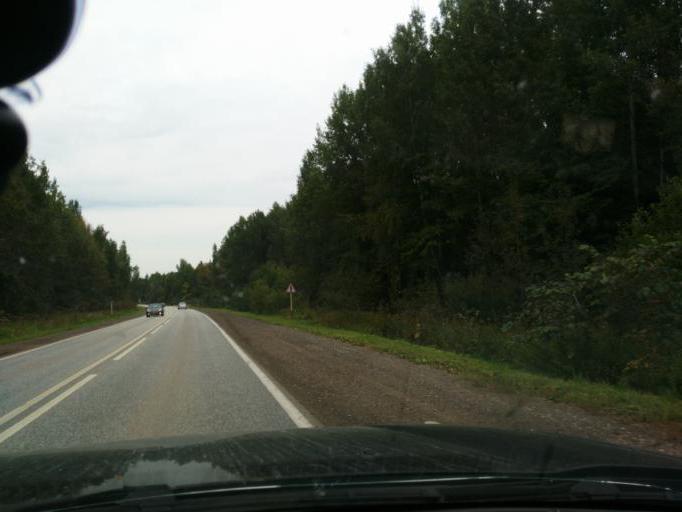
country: RU
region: Perm
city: Chernushka
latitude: 56.5934
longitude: 56.1568
